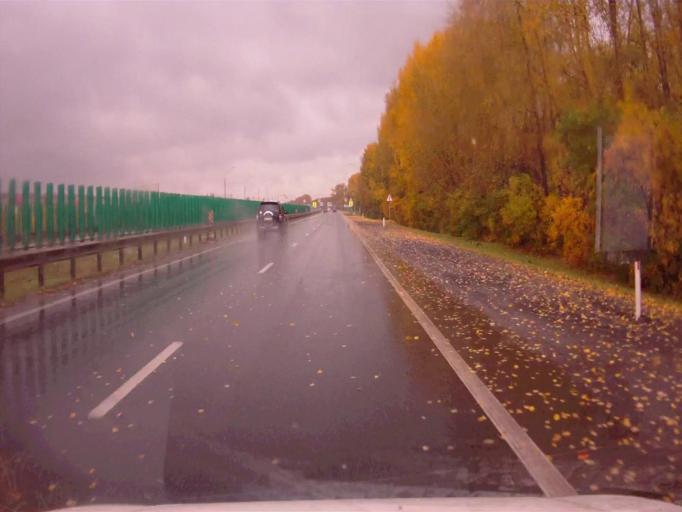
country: RU
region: Chelyabinsk
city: Dolgoderevenskoye
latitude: 55.2805
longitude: 61.3433
